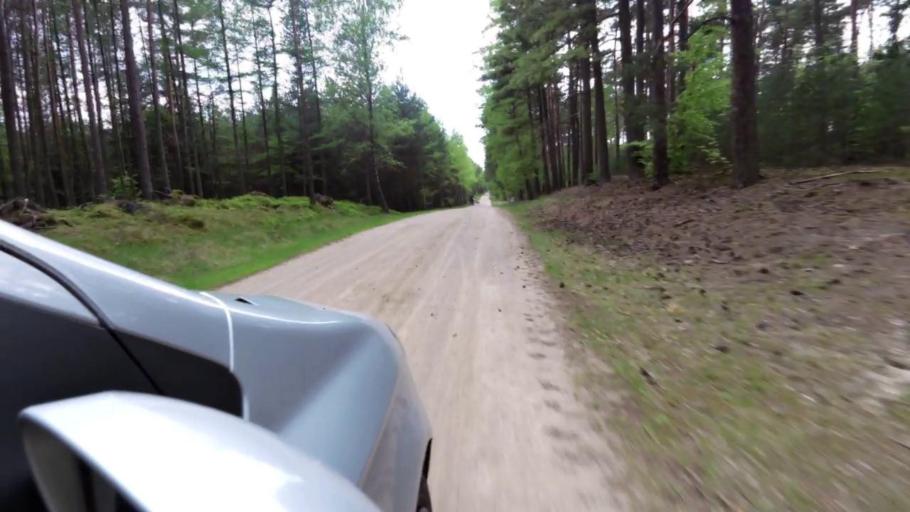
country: PL
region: West Pomeranian Voivodeship
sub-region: Powiat walecki
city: Walcz
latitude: 53.2709
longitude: 16.3926
